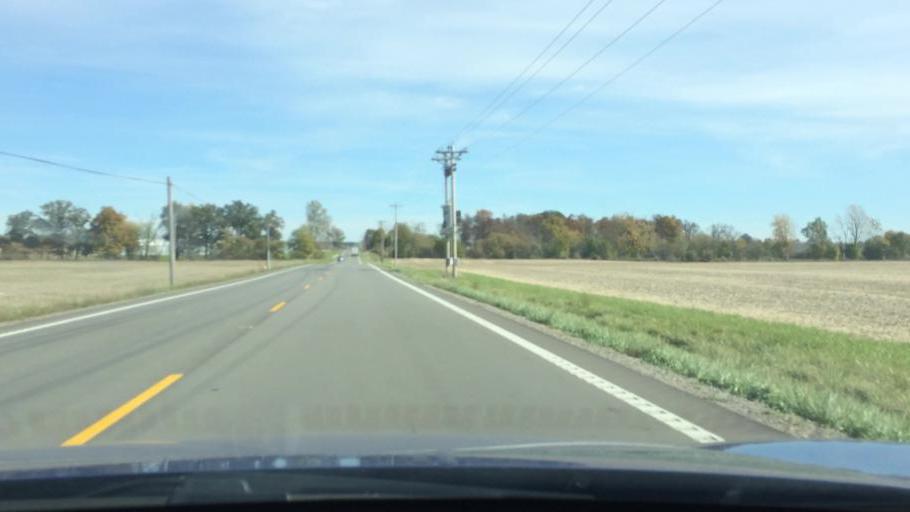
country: US
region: Ohio
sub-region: Logan County
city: Russells Point
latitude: 40.4440
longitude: -83.8386
